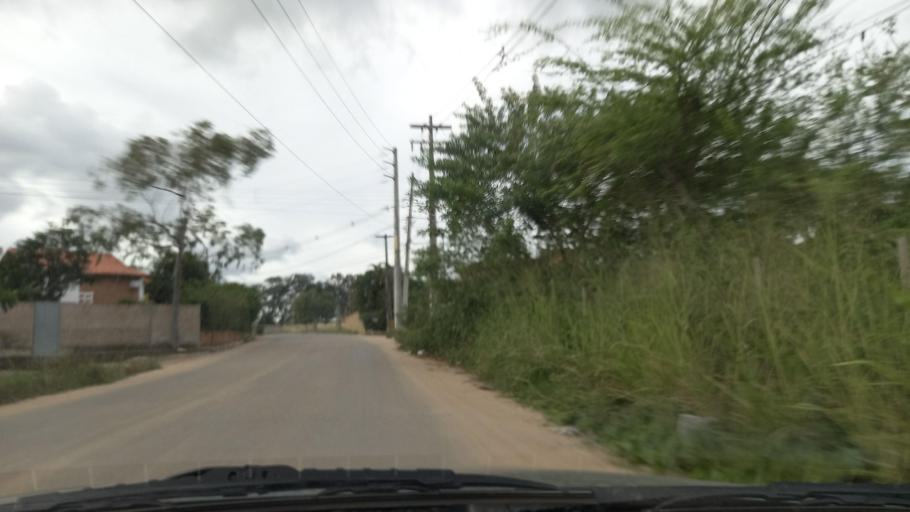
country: BR
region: Pernambuco
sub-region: Gravata
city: Gravata
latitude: -8.1964
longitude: -35.5413
